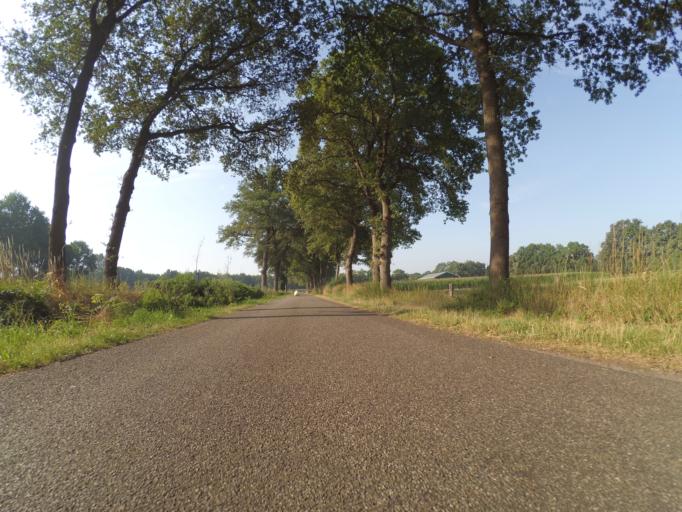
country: NL
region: Overijssel
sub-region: Gemeente Borne
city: Borne
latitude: 52.3406
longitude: 6.7920
